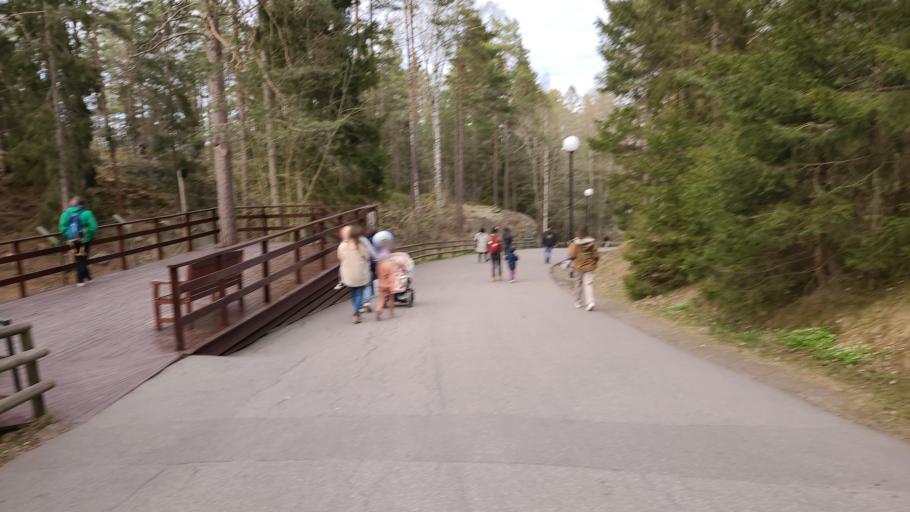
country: SE
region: OEstergoetland
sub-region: Norrkopings Kommun
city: Krokek
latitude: 58.6646
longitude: 16.4627
